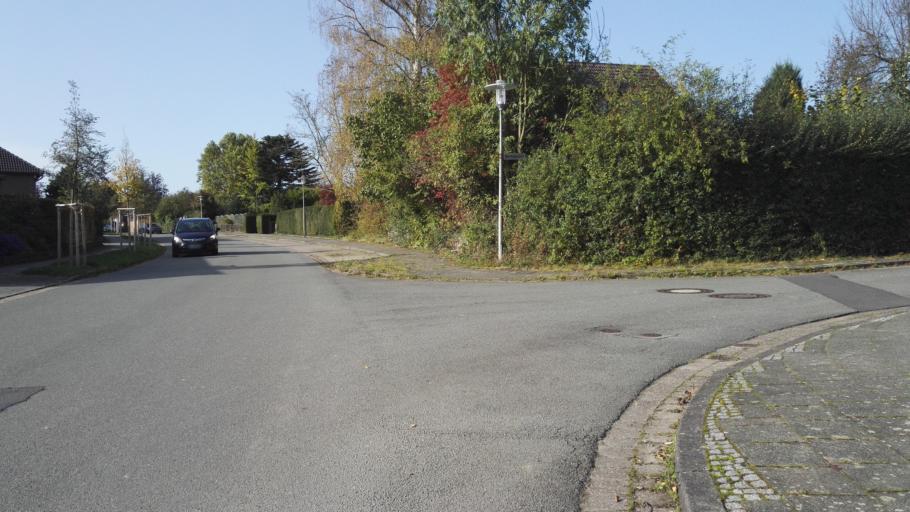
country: DE
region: Lower Saxony
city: Hildesheim
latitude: 52.1154
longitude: 9.9964
